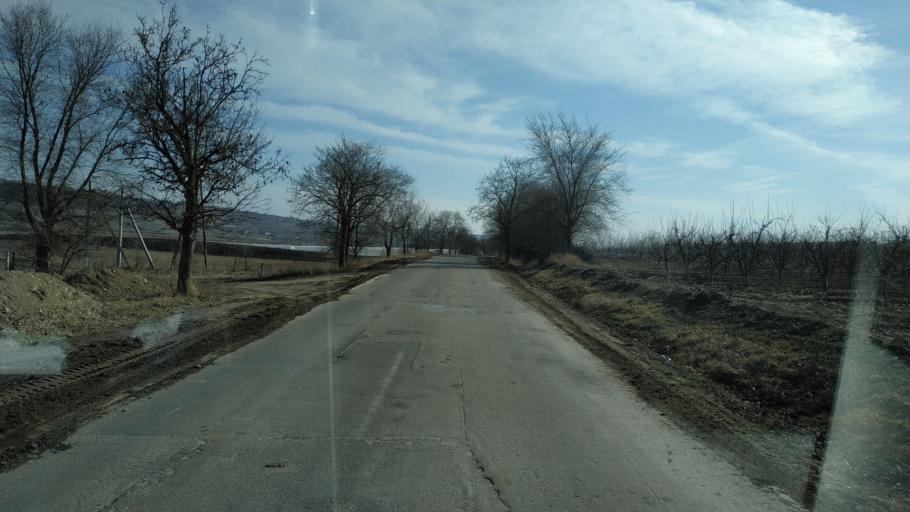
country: MD
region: Nisporeni
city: Nisporeni
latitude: 47.0837
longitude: 28.1423
